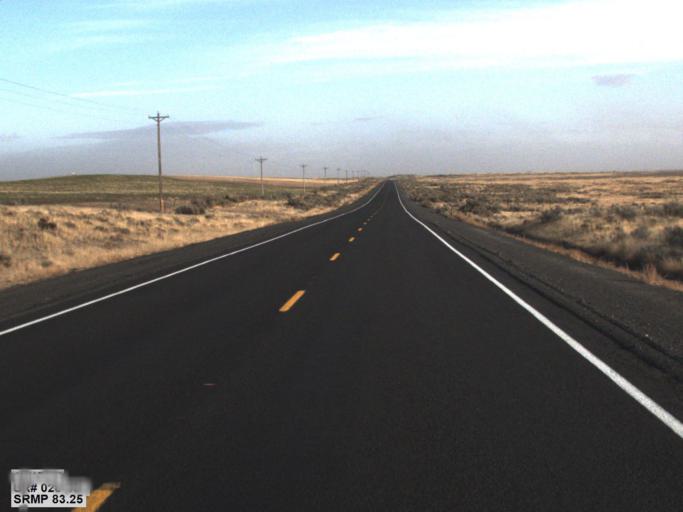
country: US
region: Washington
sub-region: Grant County
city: Warden
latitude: 47.3376
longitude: -118.8996
